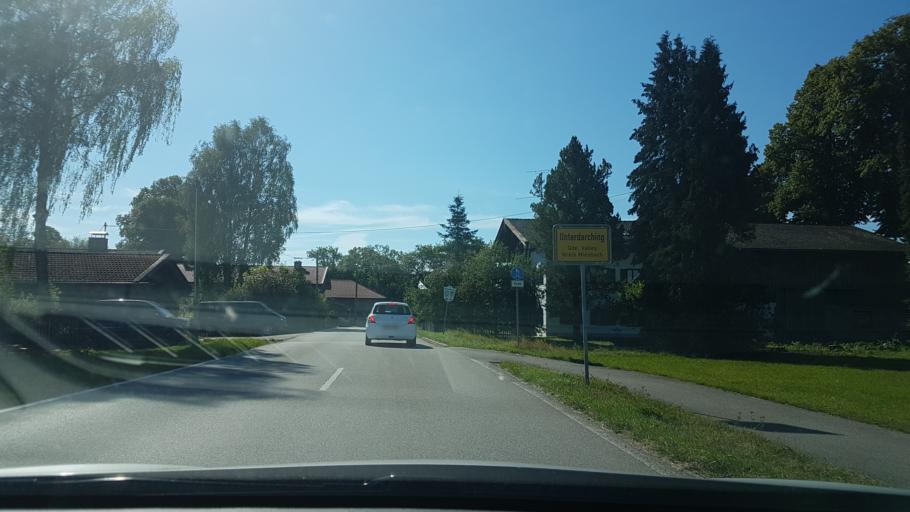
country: DE
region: Bavaria
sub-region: Upper Bavaria
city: Valley
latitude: 47.8914
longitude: 11.7675
